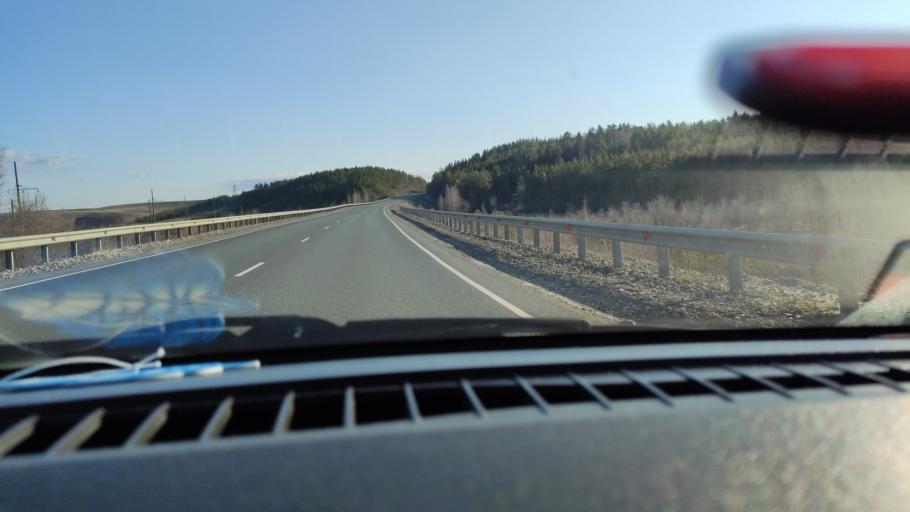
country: RU
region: Saratov
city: Khvalynsk
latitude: 52.5296
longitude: 48.0278
